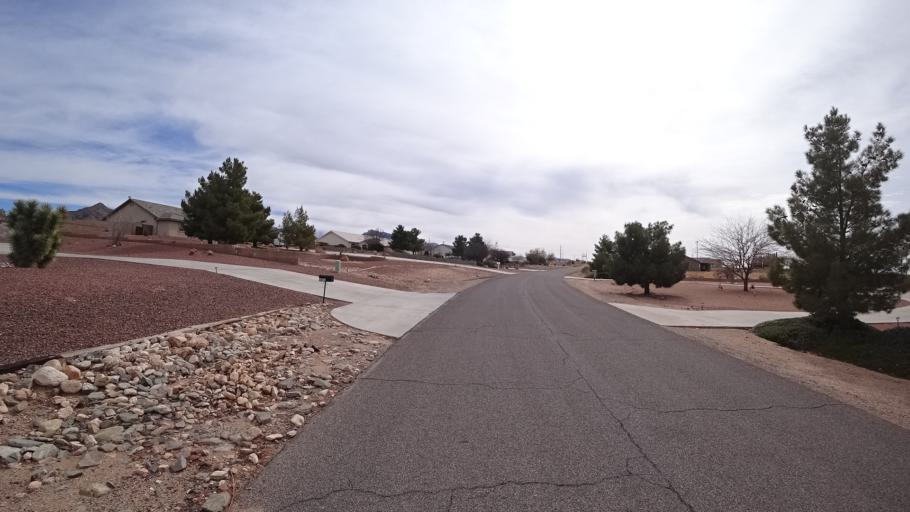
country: US
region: Arizona
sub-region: Mohave County
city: Kingman
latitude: 35.1836
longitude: -113.9803
